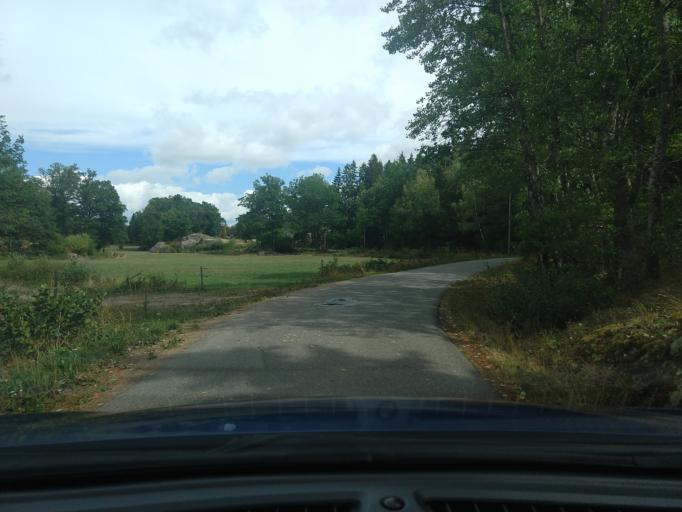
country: SE
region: Blekinge
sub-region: Ronneby Kommun
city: Brakne-Hoby
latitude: 56.2909
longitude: 15.1939
